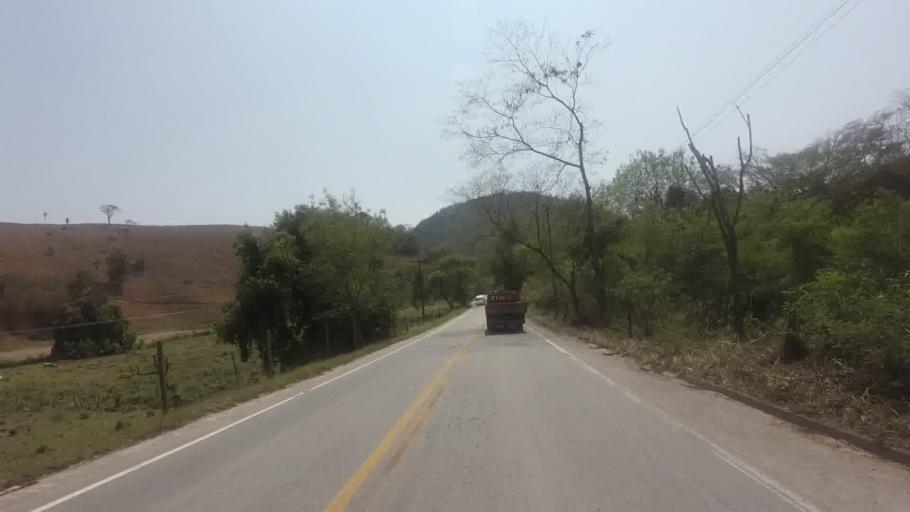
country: BR
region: Espirito Santo
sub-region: Cachoeiro De Itapemirim
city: Cachoeiro de Itapemirim
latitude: -20.8696
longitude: -41.0379
